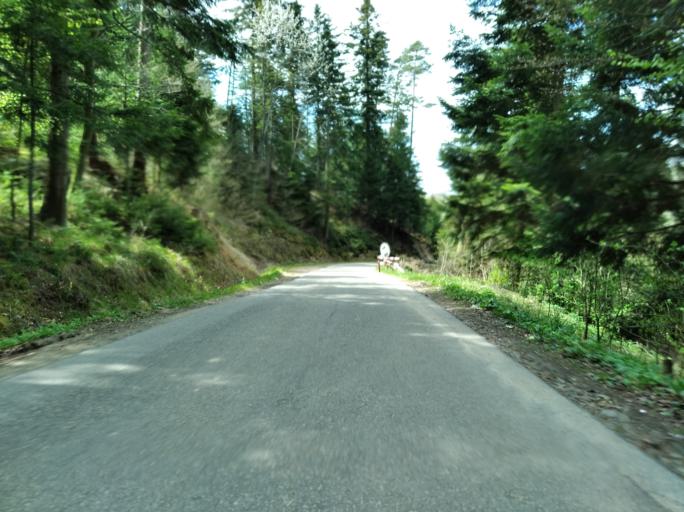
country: PL
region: Subcarpathian Voivodeship
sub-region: Powiat brzozowski
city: Wesola
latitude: 49.7580
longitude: 22.1235
